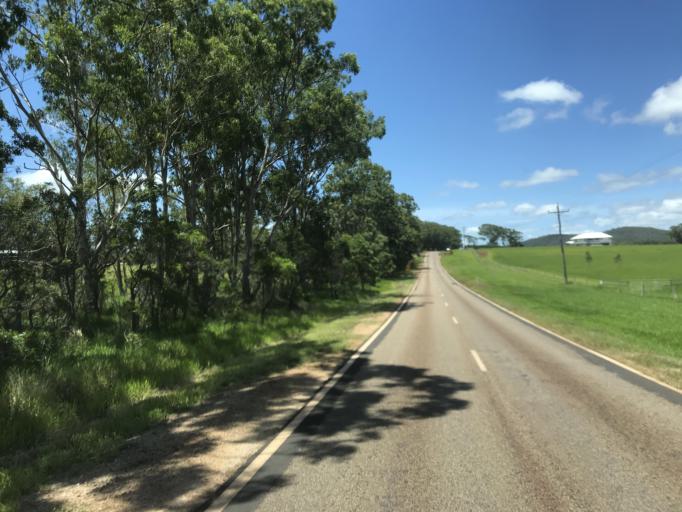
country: AU
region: Queensland
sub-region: Tablelands
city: Ravenshoe
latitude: -17.5178
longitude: 145.4512
